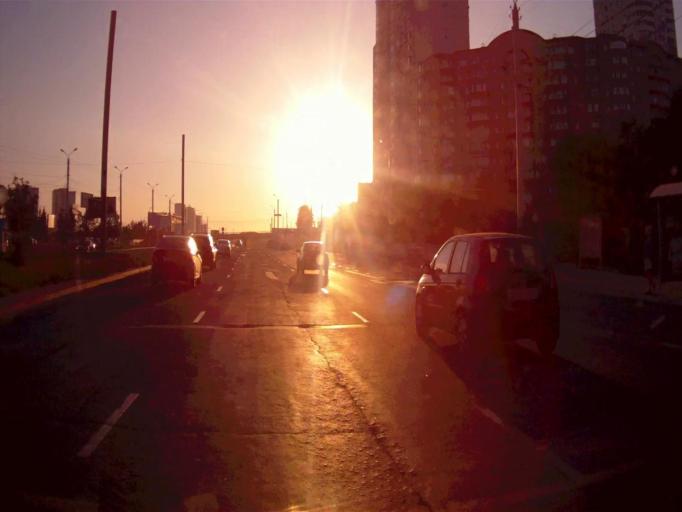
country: RU
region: Chelyabinsk
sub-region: Gorod Chelyabinsk
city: Chelyabinsk
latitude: 55.1744
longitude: 61.3930
